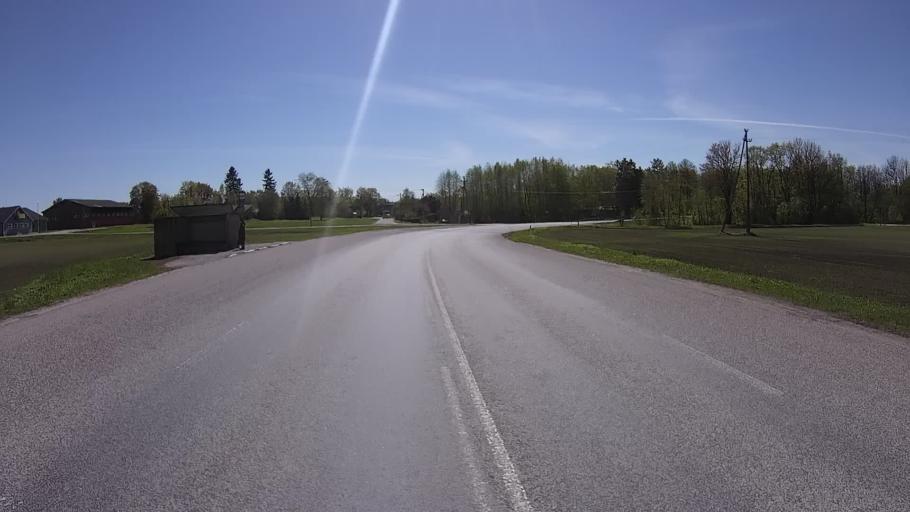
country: EE
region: Harju
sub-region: Anija vald
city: Kehra
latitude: 59.1291
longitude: 25.2044
